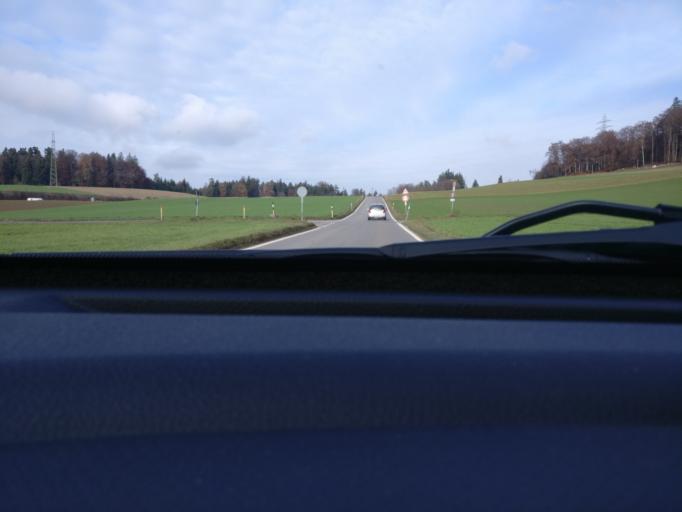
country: CH
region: Bern
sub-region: Bern-Mittelland District
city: Bolligen
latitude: 46.9884
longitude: 7.4816
